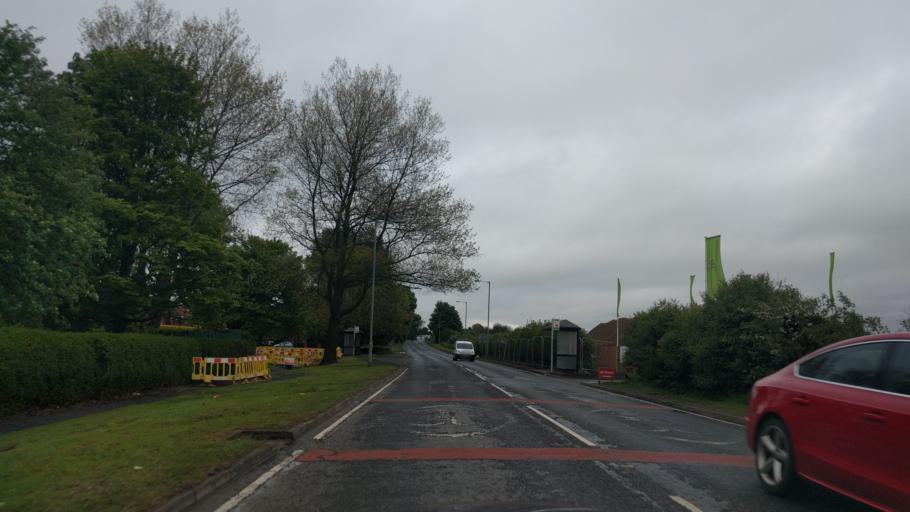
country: GB
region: England
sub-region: Northumberland
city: Morpeth
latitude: 55.1582
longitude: -1.6714
